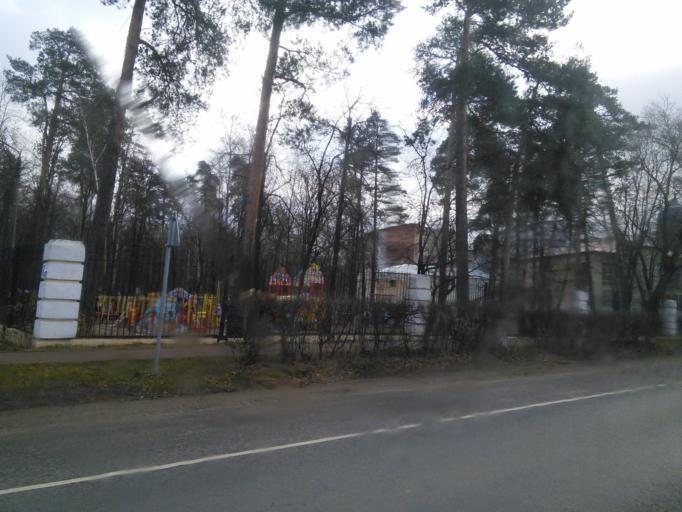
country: RU
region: Moskovskaya
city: Likino-Dulevo
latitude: 55.7071
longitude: 38.9577
